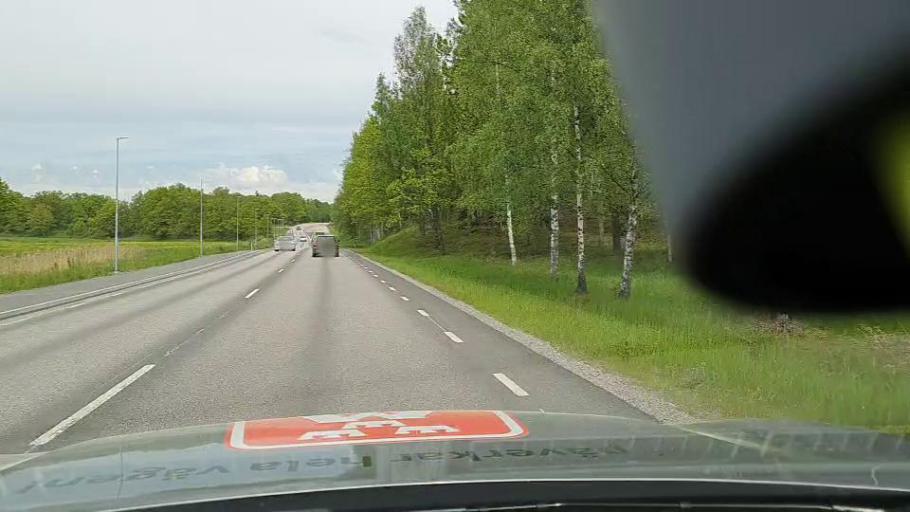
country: SE
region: Soedermanland
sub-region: Flens Kommun
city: Flen
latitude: 59.0759
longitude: 16.5959
